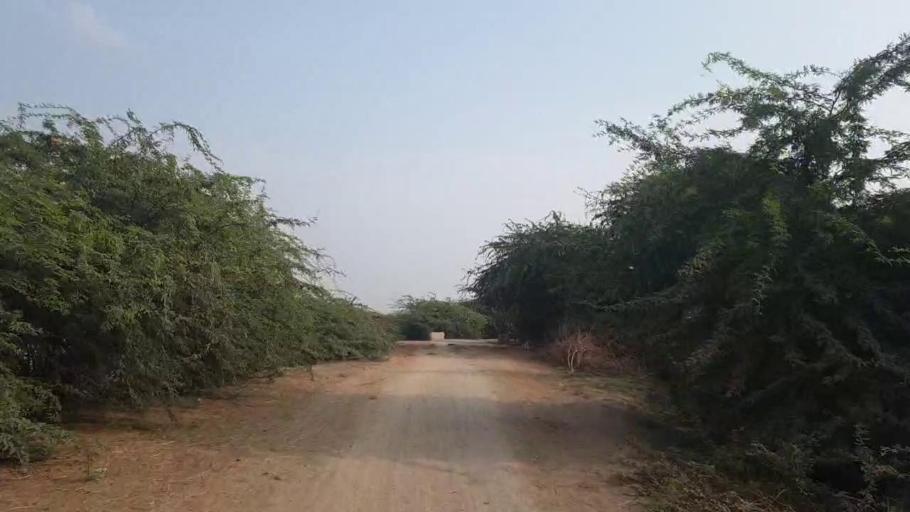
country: PK
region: Sindh
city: Badin
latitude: 24.6098
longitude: 68.6869
